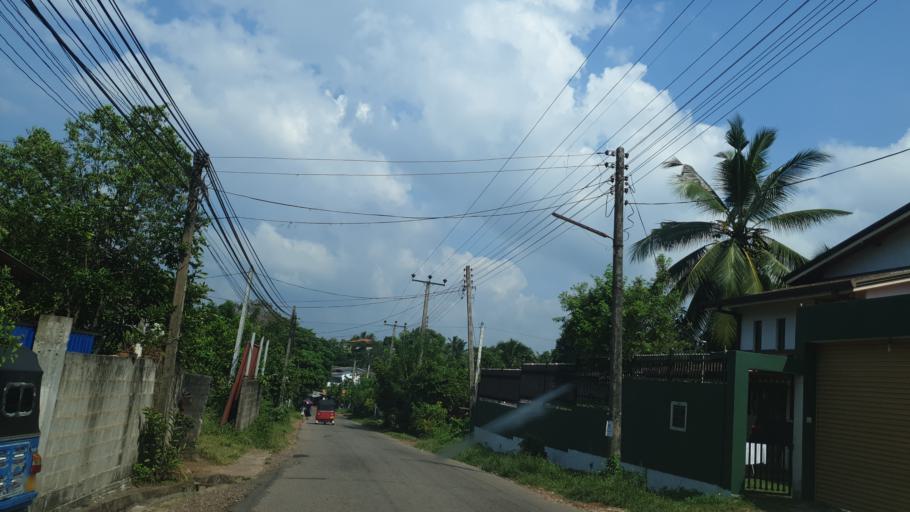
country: LK
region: Western
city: Panadura
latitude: 6.7356
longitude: 79.9382
